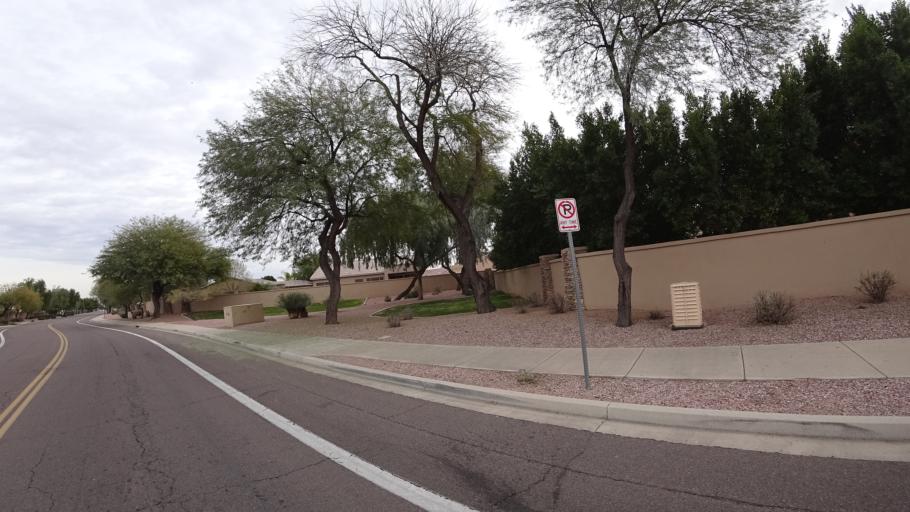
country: US
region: Arizona
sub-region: Maricopa County
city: Peoria
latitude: 33.6471
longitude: -112.1758
